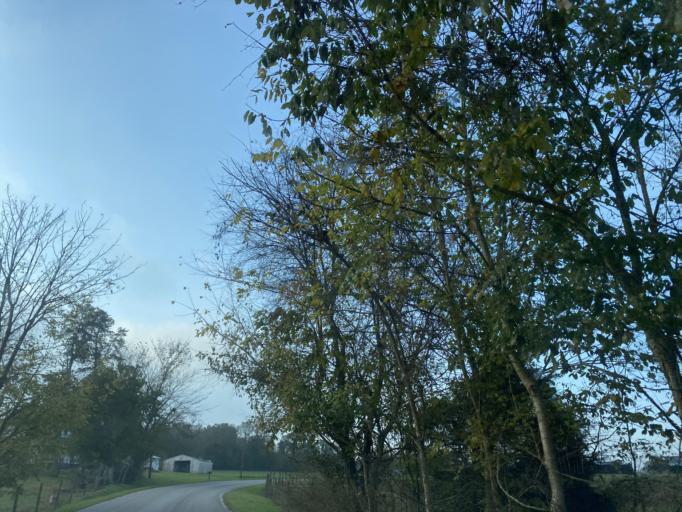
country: US
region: Kentucky
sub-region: Pendleton County
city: Falmouth
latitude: 38.7330
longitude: -84.3161
